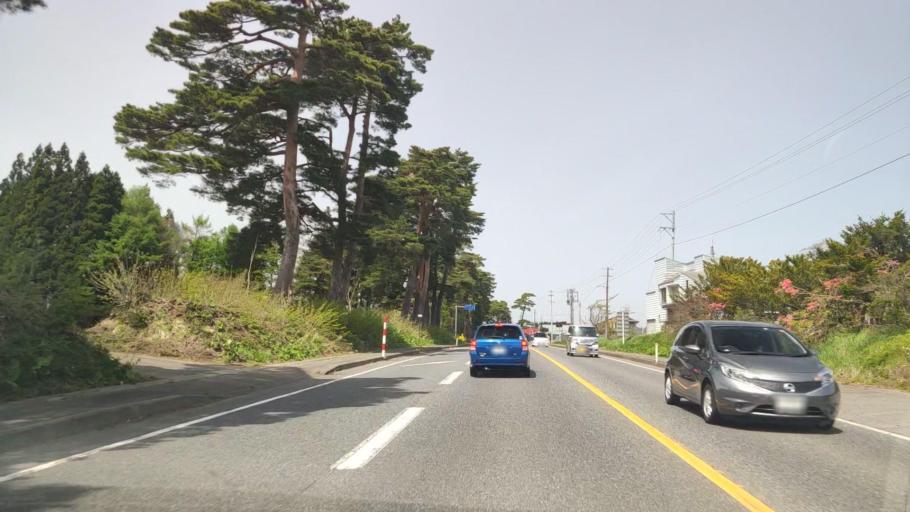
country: JP
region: Aomori
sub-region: Misawa Shi
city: Inuotose
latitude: 40.6685
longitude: 141.1848
